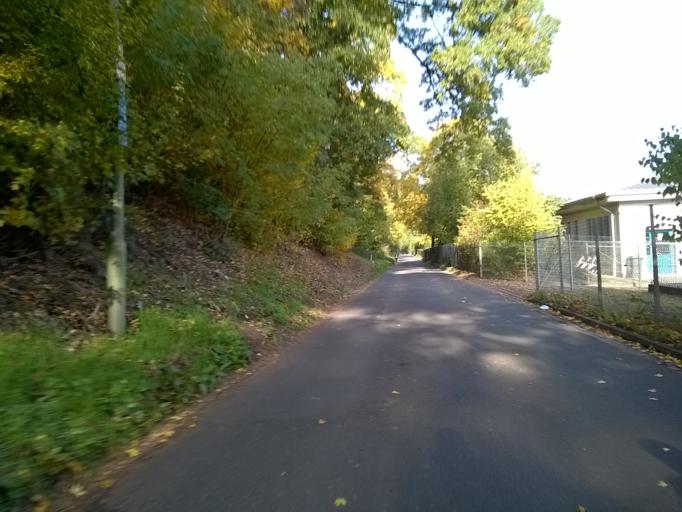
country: DE
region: Rheinland-Pfalz
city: Otterbach
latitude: 49.4590
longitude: 7.7419
